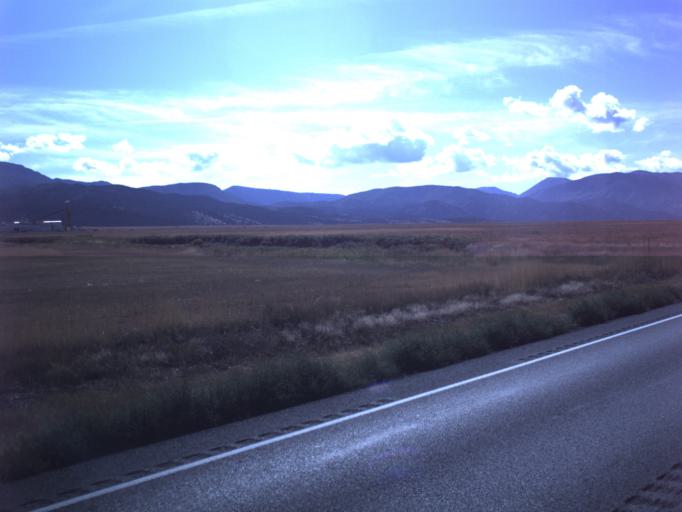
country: US
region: Utah
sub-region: Juab County
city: Nephi
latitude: 39.6373
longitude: -111.8616
